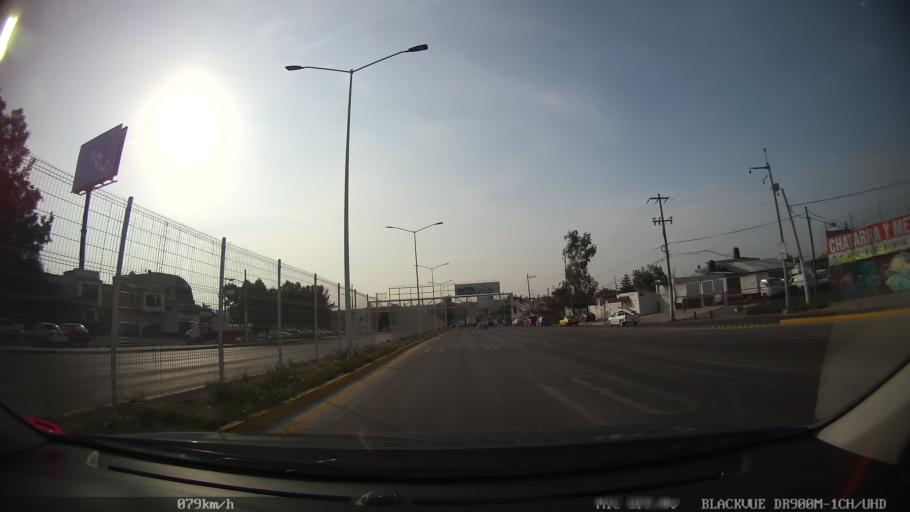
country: MX
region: Jalisco
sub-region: Zapopan
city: Zapopan
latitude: 20.7272
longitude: -103.3416
